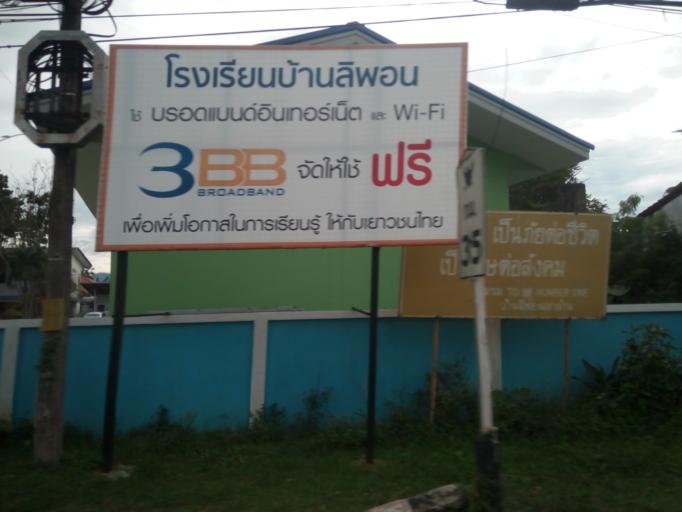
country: TH
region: Phuket
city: Thalang
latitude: 8.0036
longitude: 98.3454
